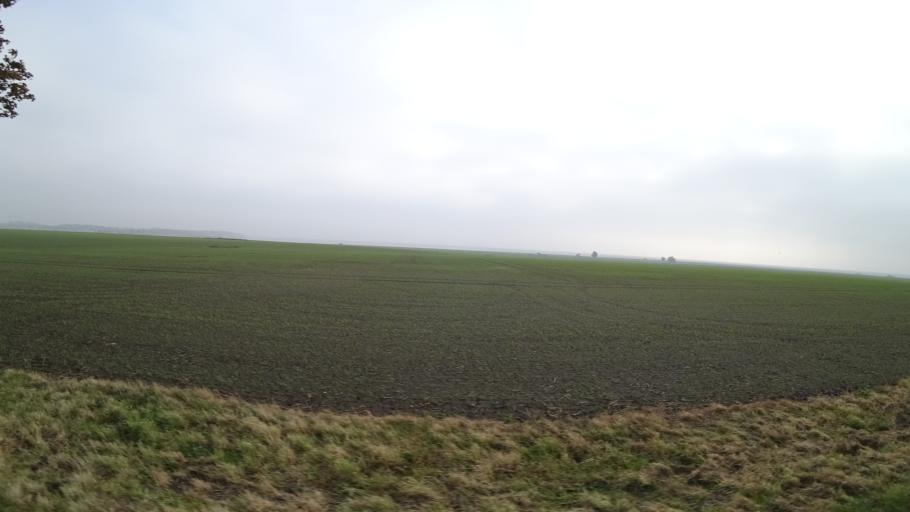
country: SE
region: Skane
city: Bjarred
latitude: 55.7350
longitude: 12.9780
